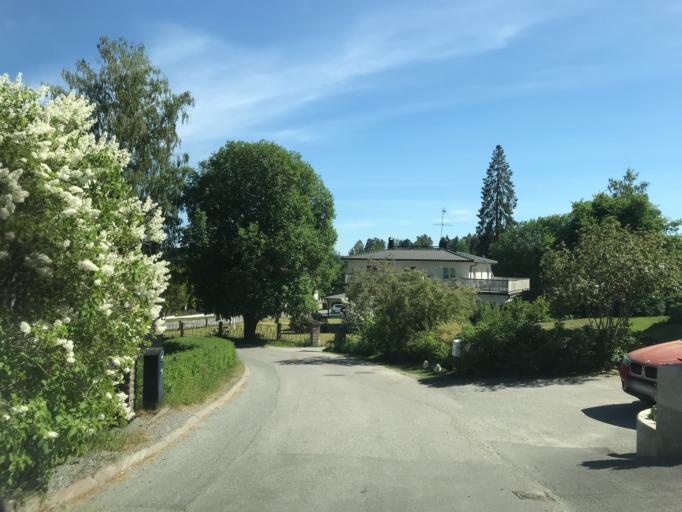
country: SE
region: Stockholm
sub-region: Sollentuna Kommun
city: Sollentuna
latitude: 59.4207
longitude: 17.9778
